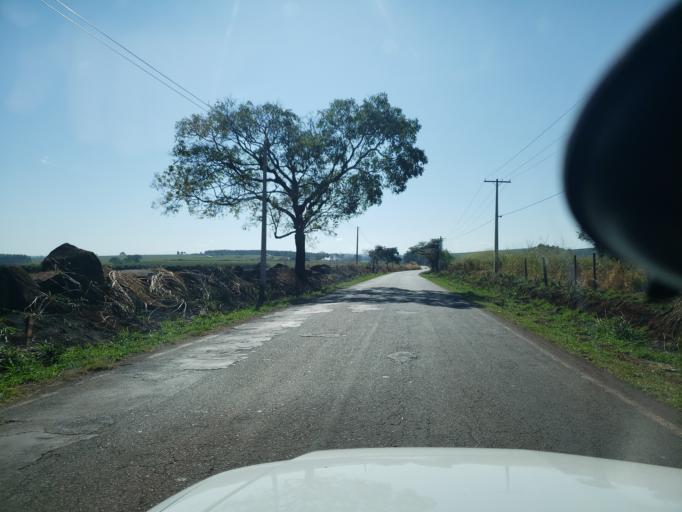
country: BR
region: Sao Paulo
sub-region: Moji-Guacu
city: Mogi-Gaucu
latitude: -22.3403
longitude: -46.8874
